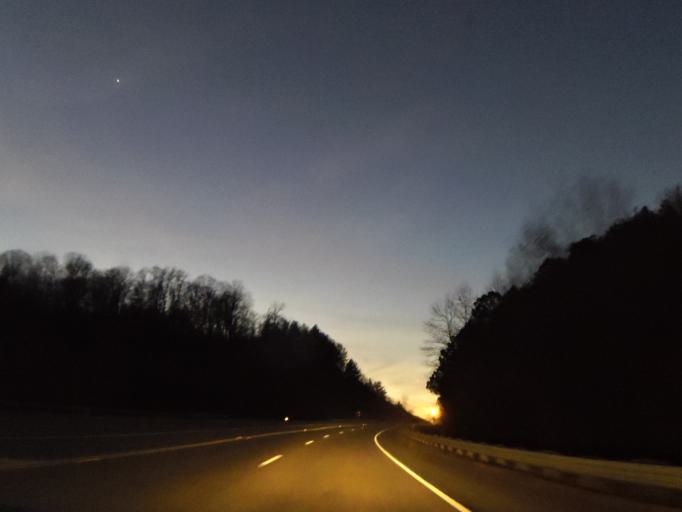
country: US
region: Georgia
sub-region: Whitfield County
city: Dalton
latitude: 34.7970
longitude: -84.9697
